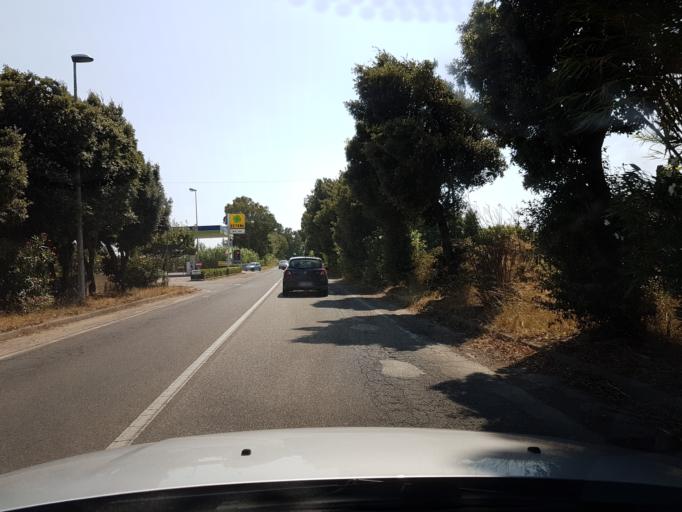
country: IT
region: Sardinia
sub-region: Provincia di Oristano
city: Donigala Fenugheddu
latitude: 39.9252
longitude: 8.5752
